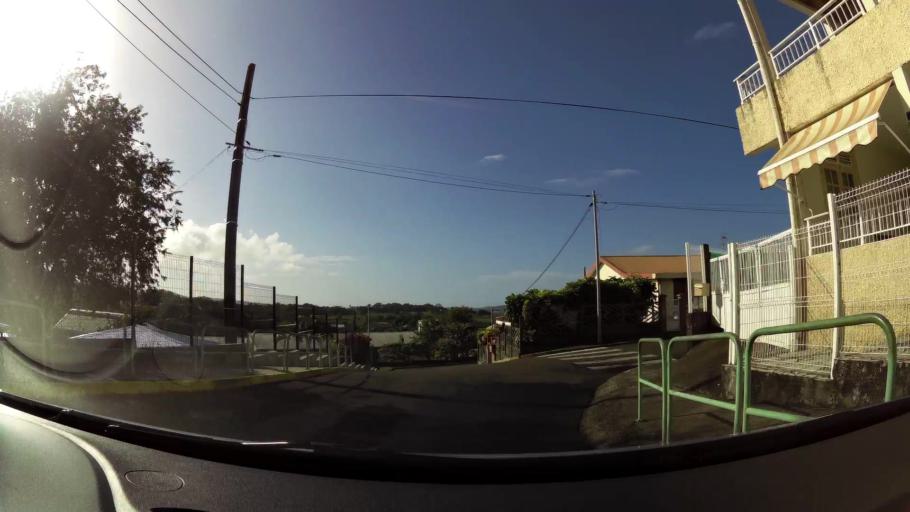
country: MQ
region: Martinique
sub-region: Martinique
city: Ducos
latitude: 14.5735
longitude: -60.9746
